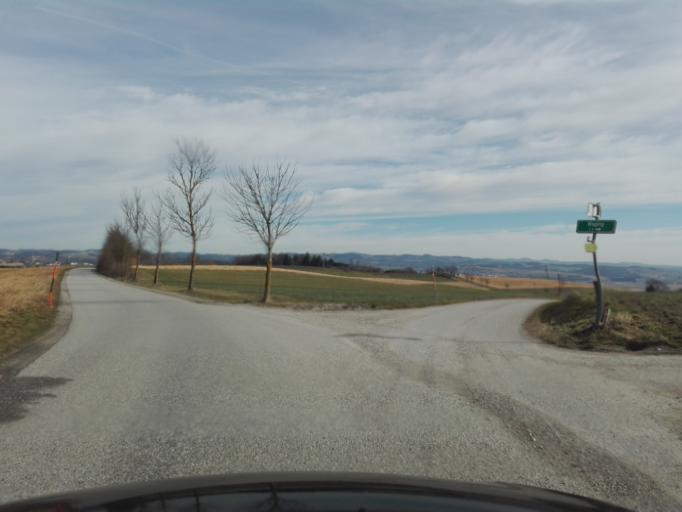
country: AT
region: Lower Austria
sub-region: Politischer Bezirk Amstetten
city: Ennsdorf
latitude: 48.2618
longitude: 14.5242
